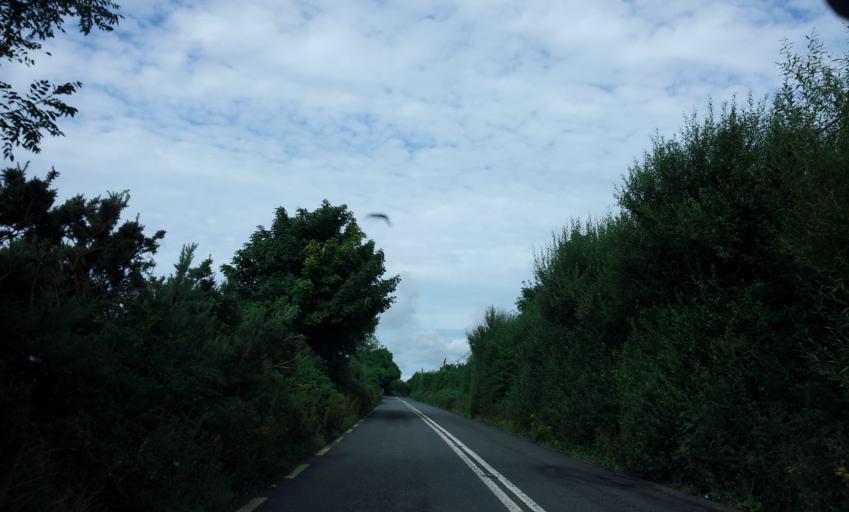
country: IE
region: Munster
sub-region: Ciarrai
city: Killorglin
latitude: 52.0827
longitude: -9.6683
